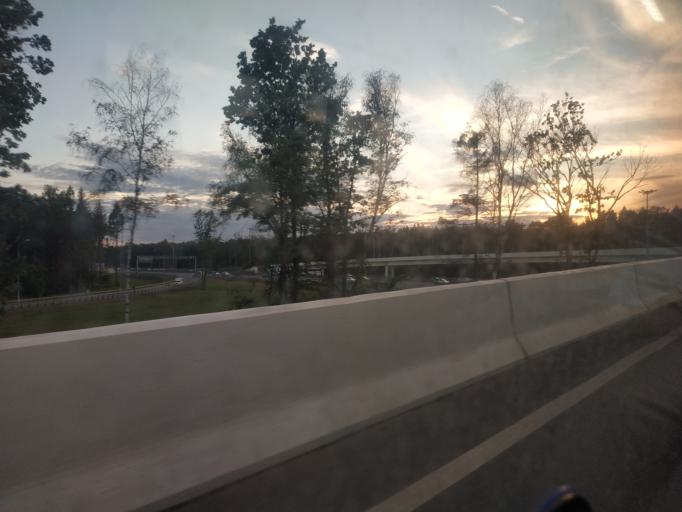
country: RU
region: Moscow
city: Solntsevo
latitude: 55.6141
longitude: 37.3780
